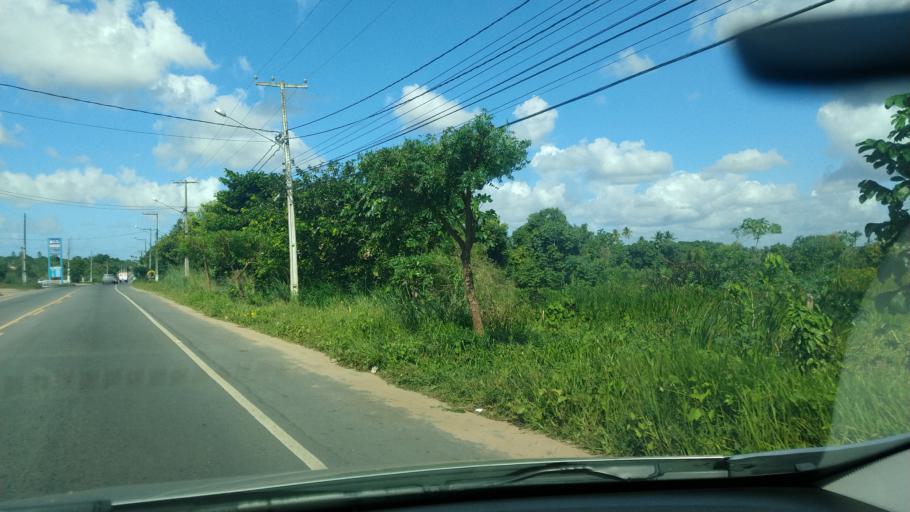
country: BR
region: Rio Grande do Norte
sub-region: Sao Goncalo Do Amarante
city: Sao Goncalo do Amarante
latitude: -5.7878
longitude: -35.3264
